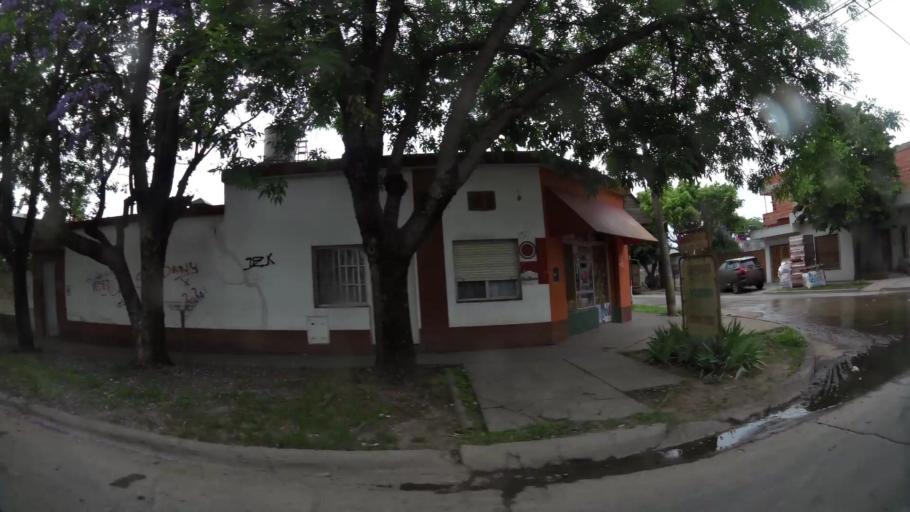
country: AR
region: Buenos Aires
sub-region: Partido de Zarate
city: Zarate
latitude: -34.0943
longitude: -59.0390
